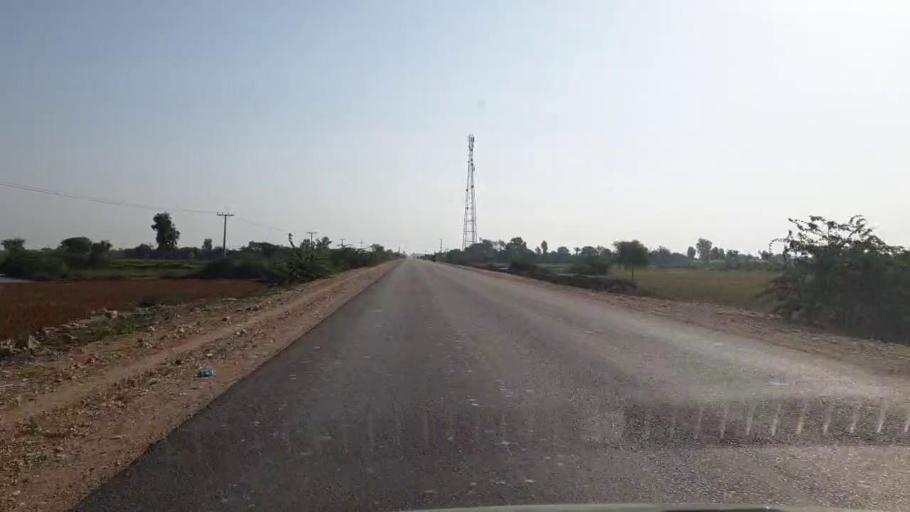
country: PK
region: Sindh
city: Badin
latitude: 24.6585
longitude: 68.9510
